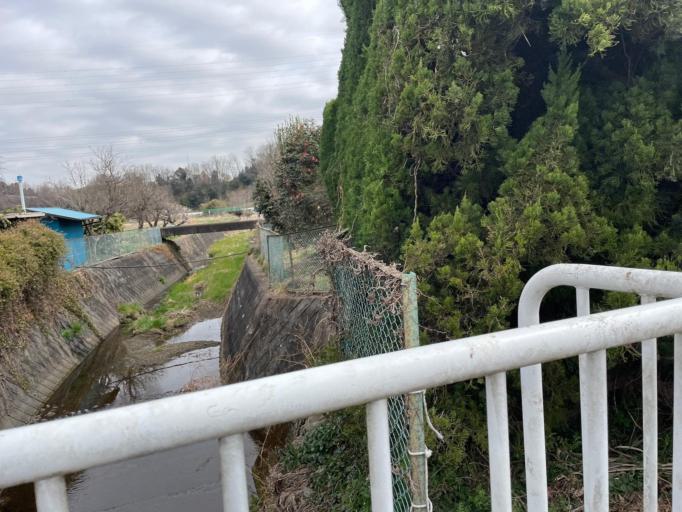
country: JP
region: Saitama
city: Ogawa
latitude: 36.0539
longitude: 139.3157
